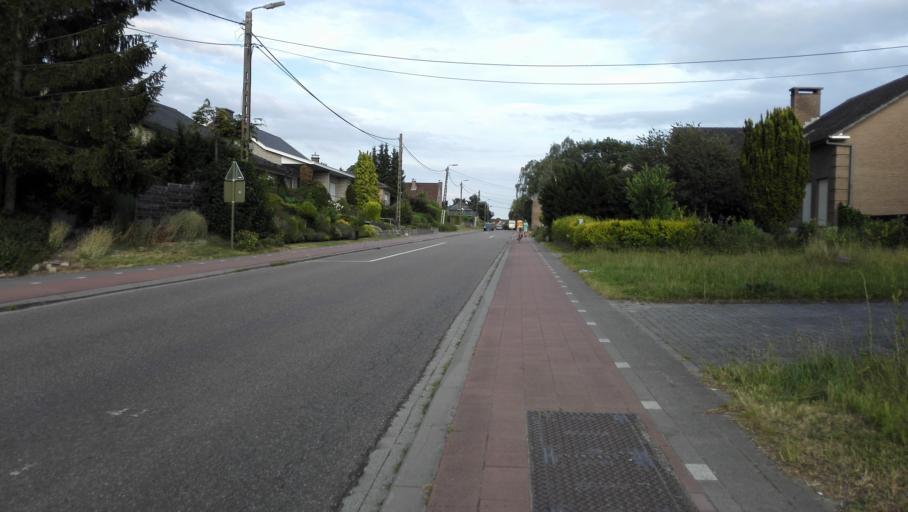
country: BE
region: Flanders
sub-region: Provincie Vlaams-Brabant
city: Bierbeek
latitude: 50.8633
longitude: 4.7446
